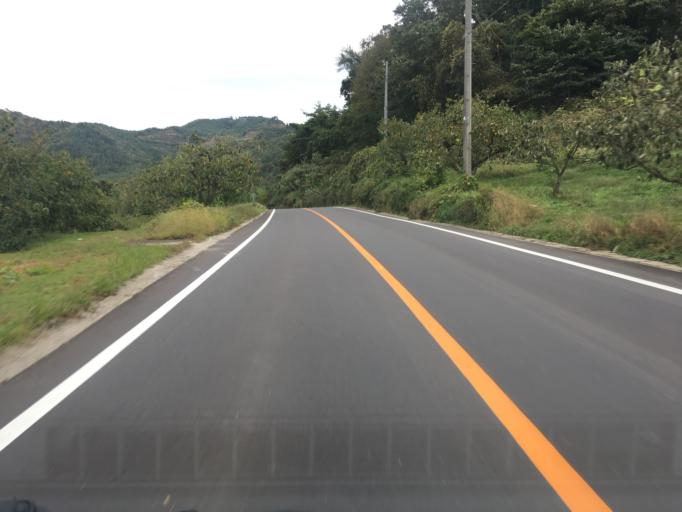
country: JP
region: Fukushima
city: Yanagawamachi-saiwaicho
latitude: 37.8725
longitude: 140.6376
